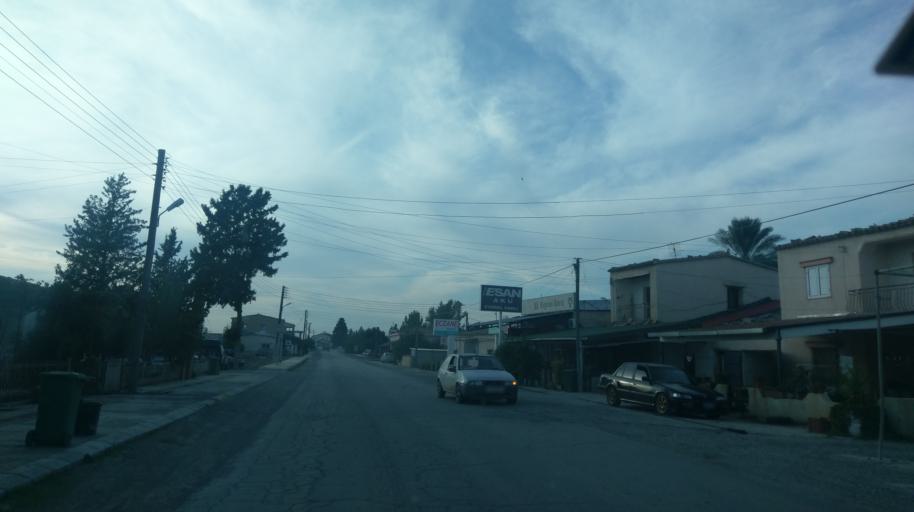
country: CY
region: Larnaka
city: Pergamos
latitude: 35.1295
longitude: 33.6588
